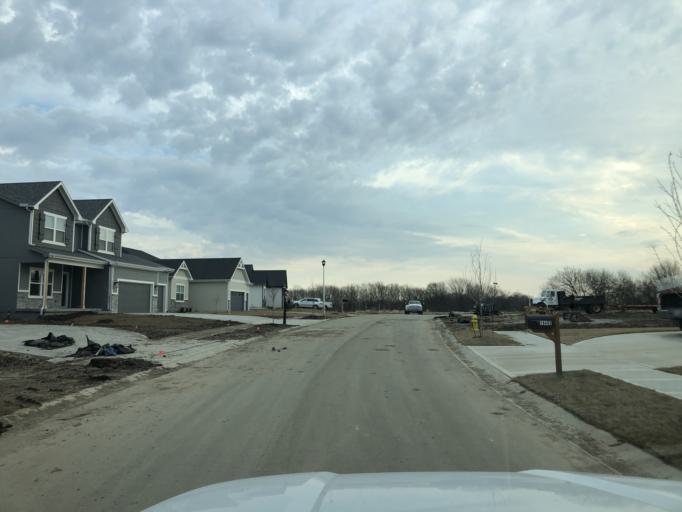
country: US
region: Kansas
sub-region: Johnson County
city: Gardner
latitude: 38.8312
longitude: -94.9572
